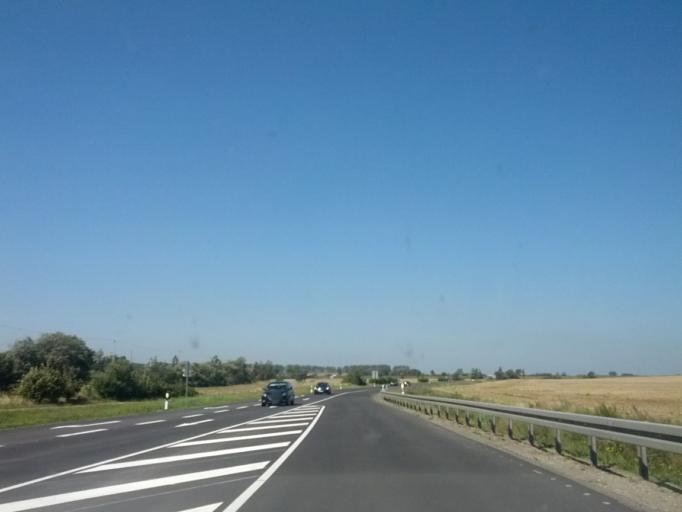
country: DE
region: Mecklenburg-Vorpommern
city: Sagard
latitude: 54.5052
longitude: 13.5486
